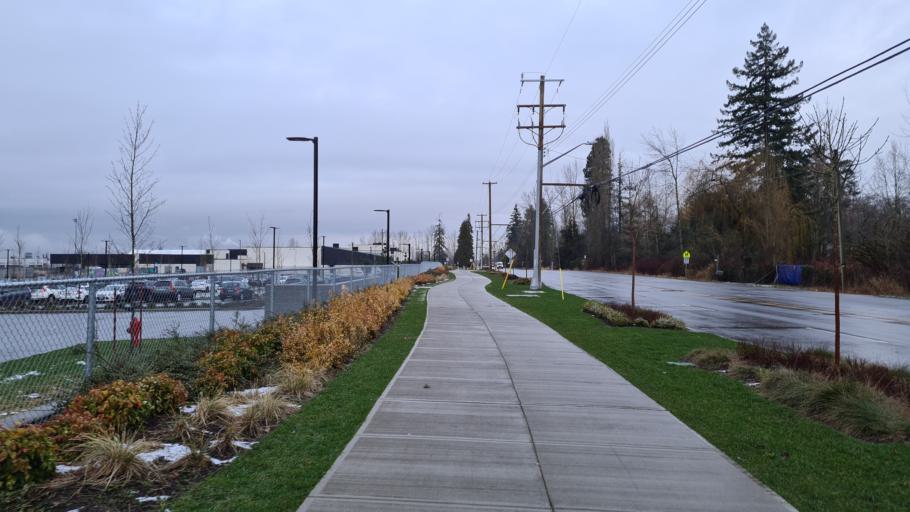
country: CA
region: British Columbia
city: Walnut Grove
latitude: 49.1417
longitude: -122.6617
